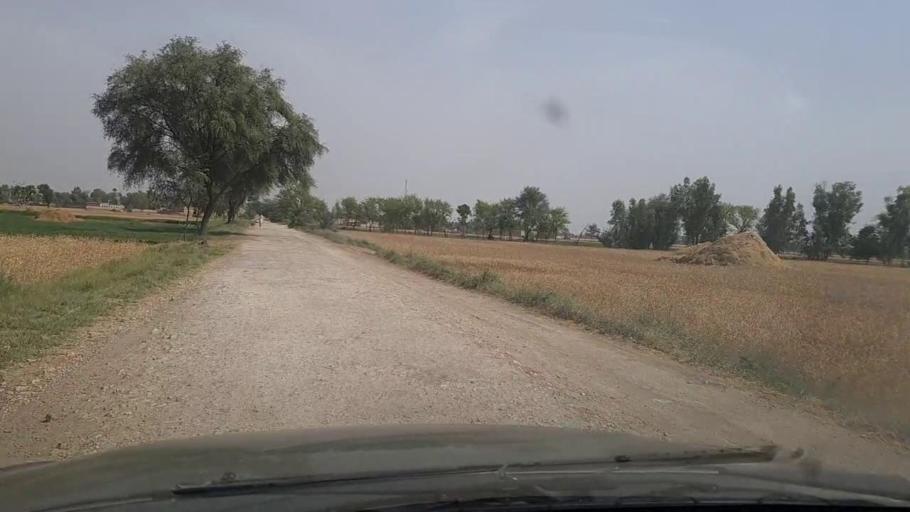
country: PK
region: Sindh
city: Chak
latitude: 27.8341
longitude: 68.7709
